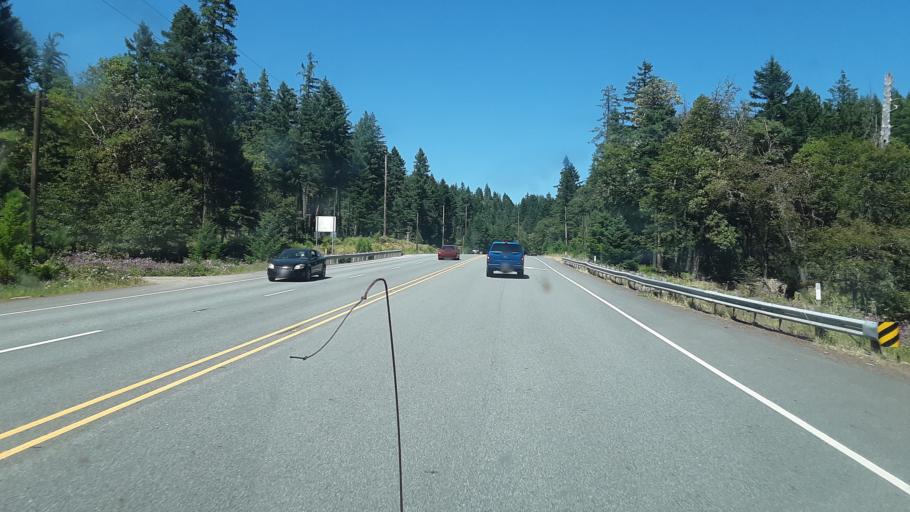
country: US
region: Oregon
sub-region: Josephine County
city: Cave Junction
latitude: 42.3308
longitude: -123.5909
